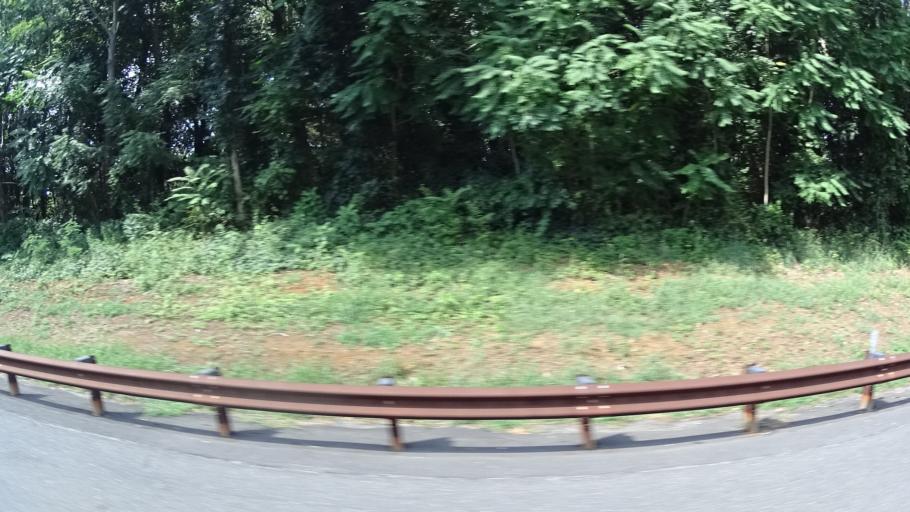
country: US
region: New Jersey
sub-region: Monmouth County
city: Tinton Falls
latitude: 40.3117
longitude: -74.0964
